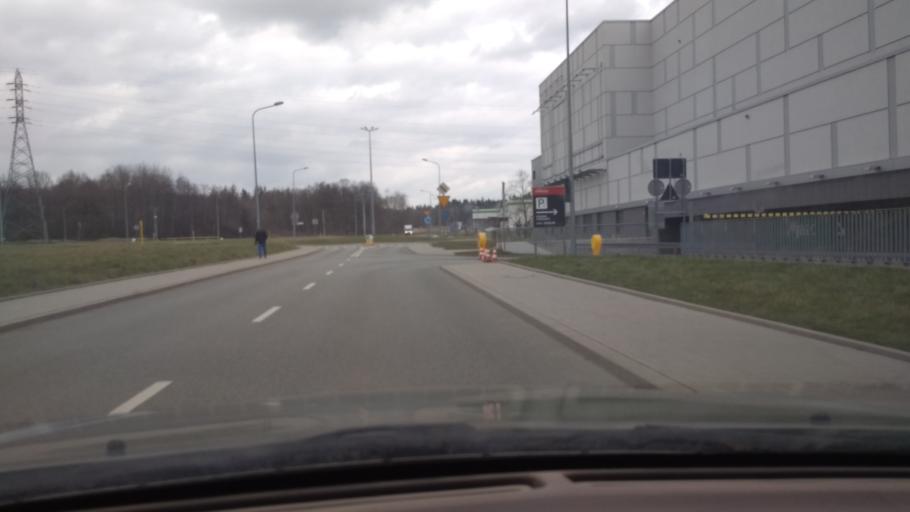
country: PL
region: Lower Silesian Voivodeship
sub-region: Powiat jeleniogorski
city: Jezow Sudecki
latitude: 50.9233
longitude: 15.7624
